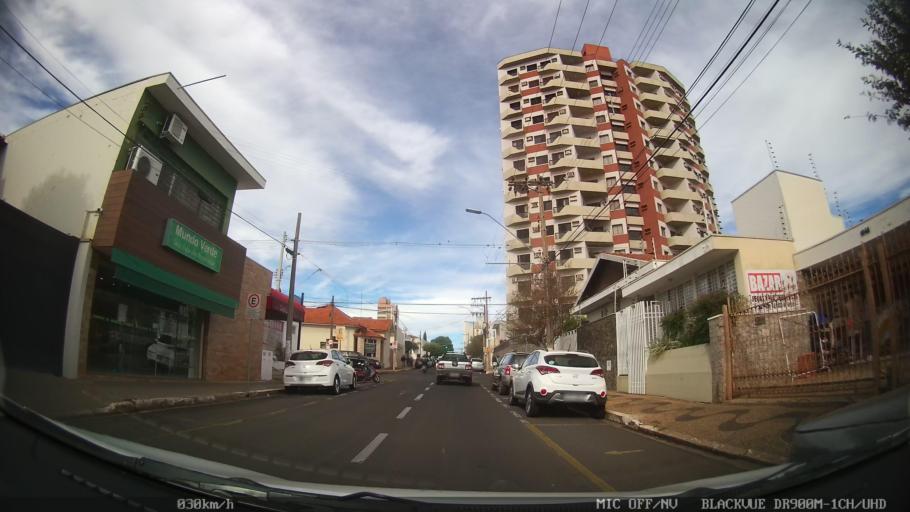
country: BR
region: Sao Paulo
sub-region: Catanduva
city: Catanduva
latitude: -21.1400
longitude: -48.9749
